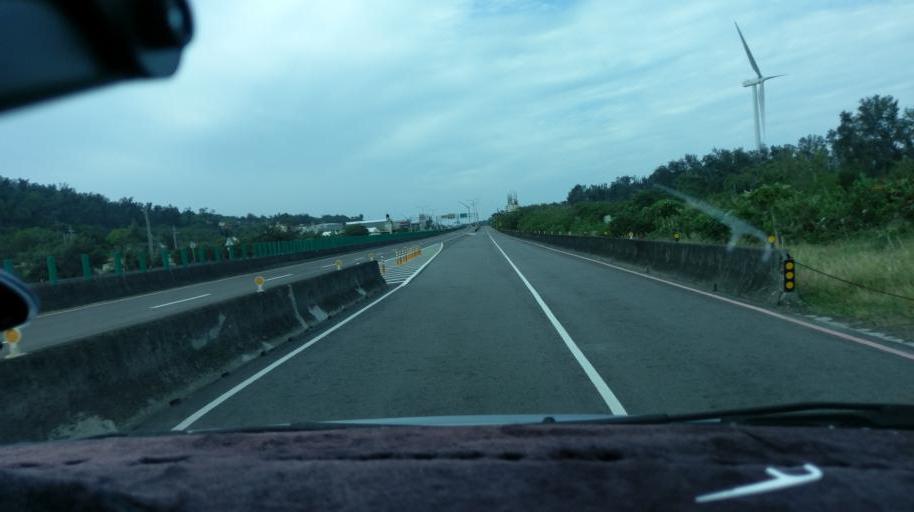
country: TW
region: Taiwan
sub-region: Hsinchu
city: Hsinchu
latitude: 24.7360
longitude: 120.8846
